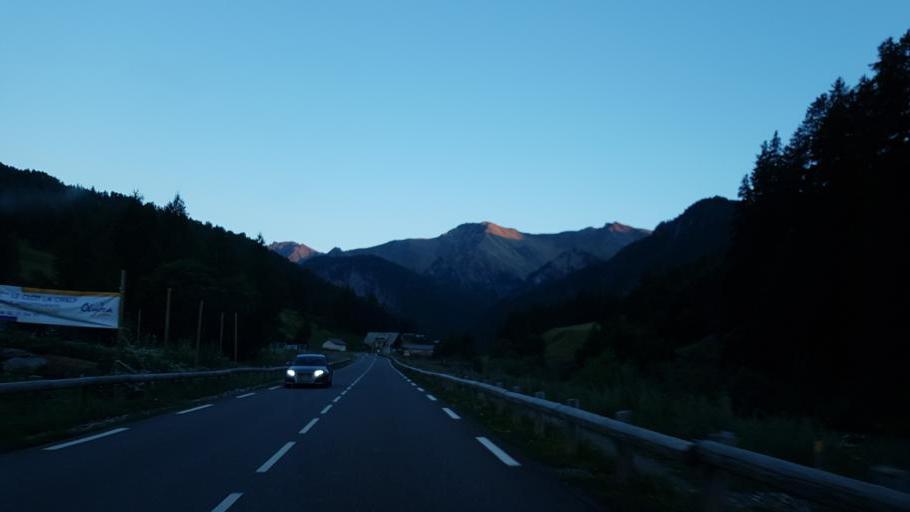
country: FR
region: Provence-Alpes-Cote d'Azur
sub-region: Departement des Hautes-Alpes
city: Guillestre
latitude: 44.7208
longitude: 6.8462
